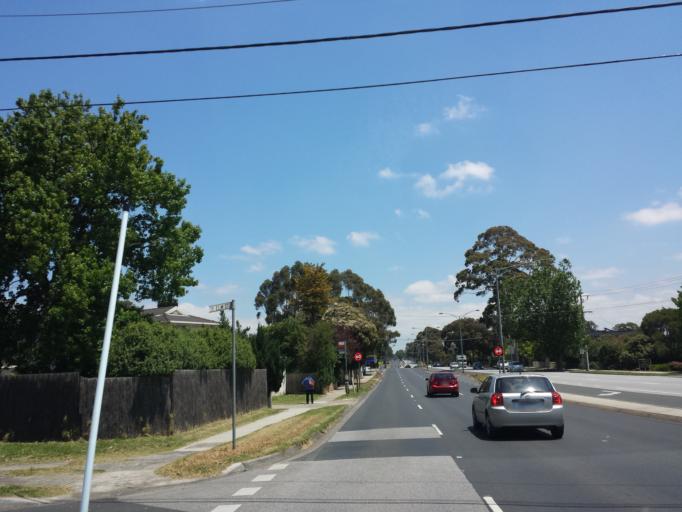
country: AU
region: Victoria
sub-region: Knox
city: Bayswater
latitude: -37.8420
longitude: 145.2613
